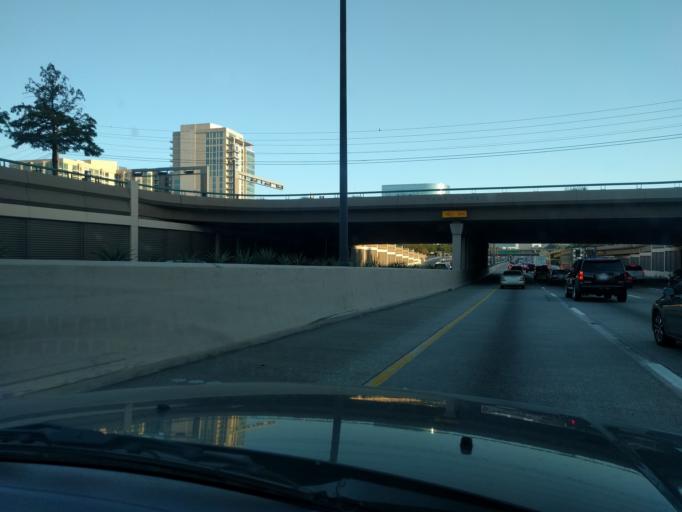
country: US
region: Texas
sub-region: Dallas County
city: University Park
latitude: 32.8725
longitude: -96.7703
